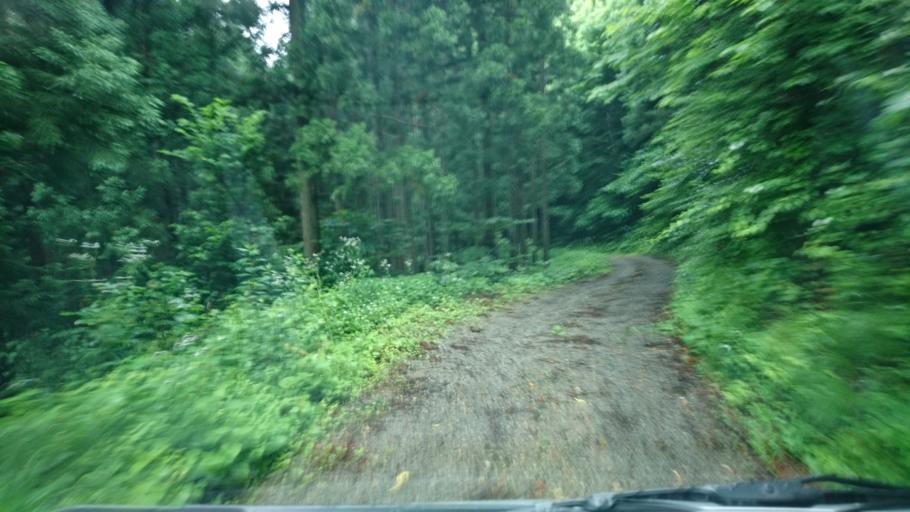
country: JP
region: Fukushima
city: Kitakata
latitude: 37.3423
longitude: 139.8153
